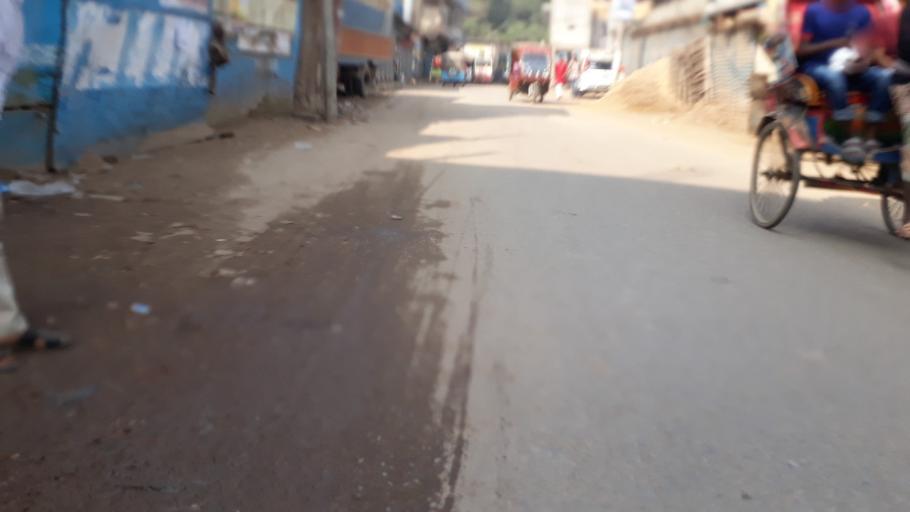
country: BD
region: Dhaka
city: Tungi
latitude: 23.8955
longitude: 90.3326
